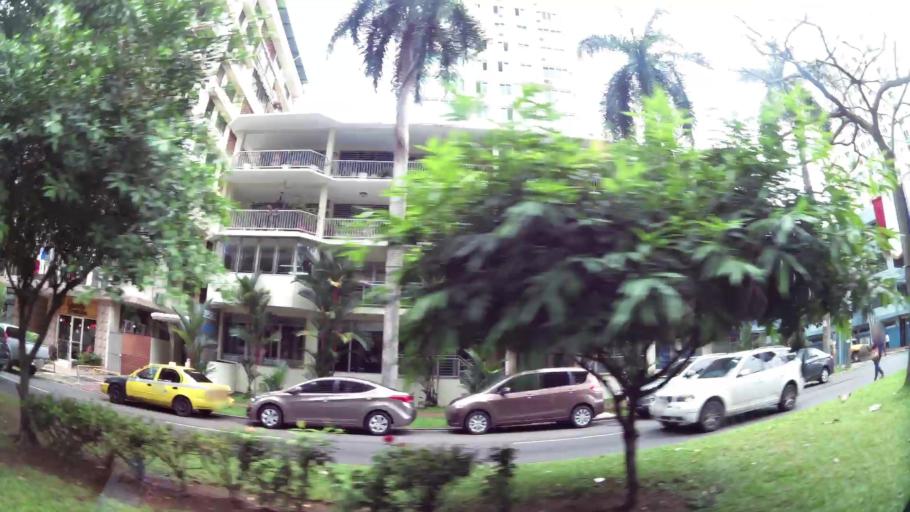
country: PA
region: Panama
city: Panama
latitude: 8.9877
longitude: -79.5301
